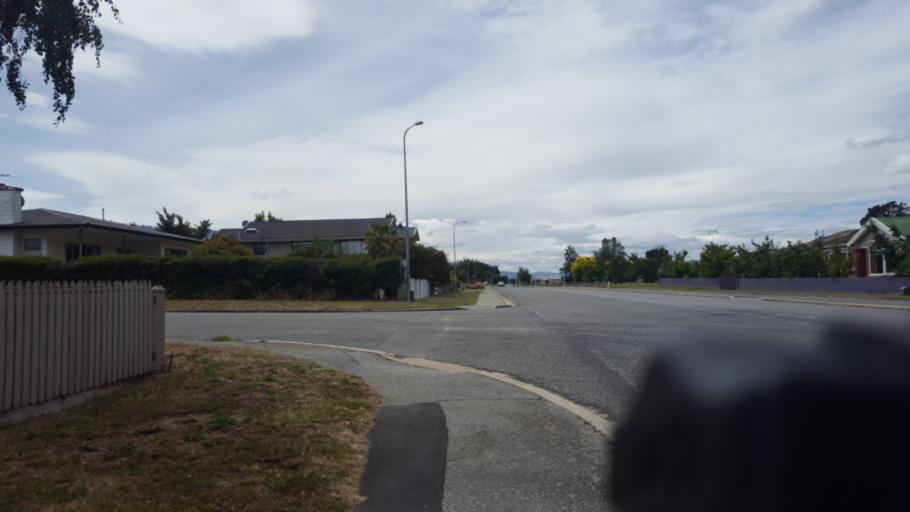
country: NZ
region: Otago
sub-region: Queenstown-Lakes District
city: Wanaka
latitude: -45.0442
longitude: 169.2132
